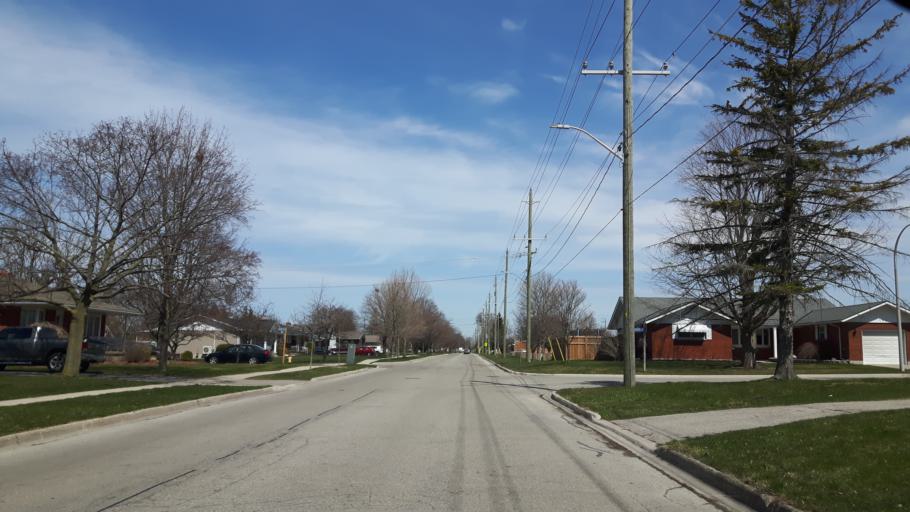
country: CA
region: Ontario
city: Goderich
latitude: 43.7310
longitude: -81.7162
